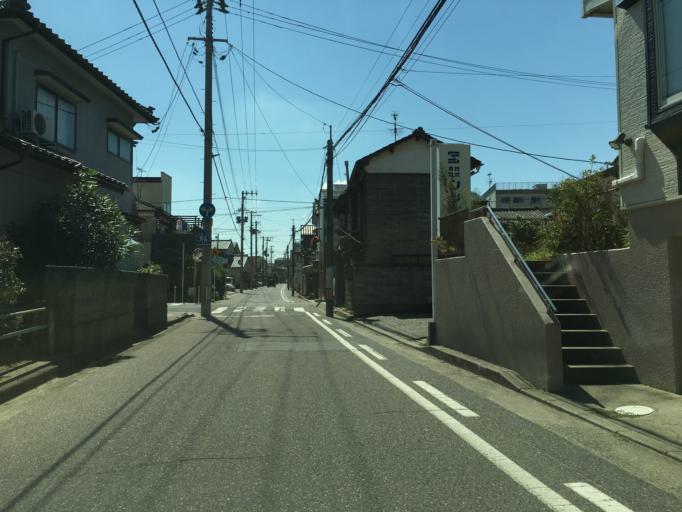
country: JP
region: Niigata
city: Niigata-shi
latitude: 37.9058
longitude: 139.0164
